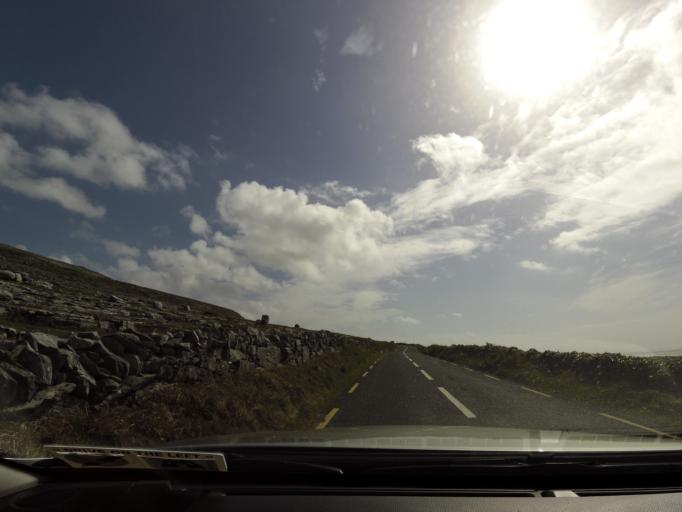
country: IE
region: Connaught
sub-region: County Galway
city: Bearna
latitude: 53.1449
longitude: -9.2729
